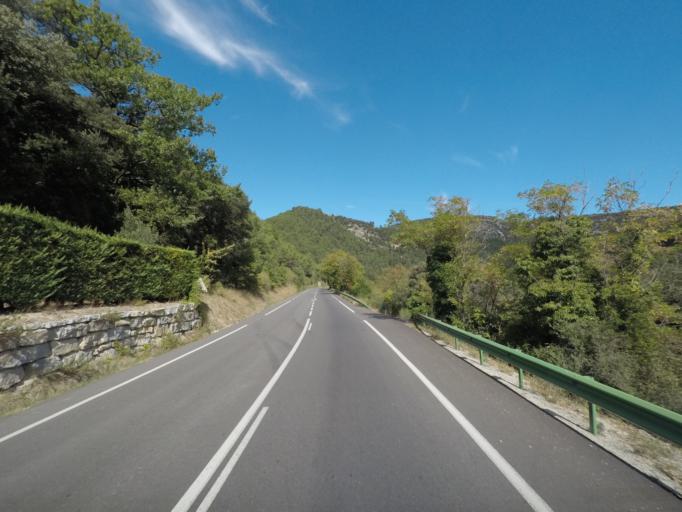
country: FR
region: Rhone-Alpes
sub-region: Departement de la Drome
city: Nyons
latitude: 44.3786
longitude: 5.1710
